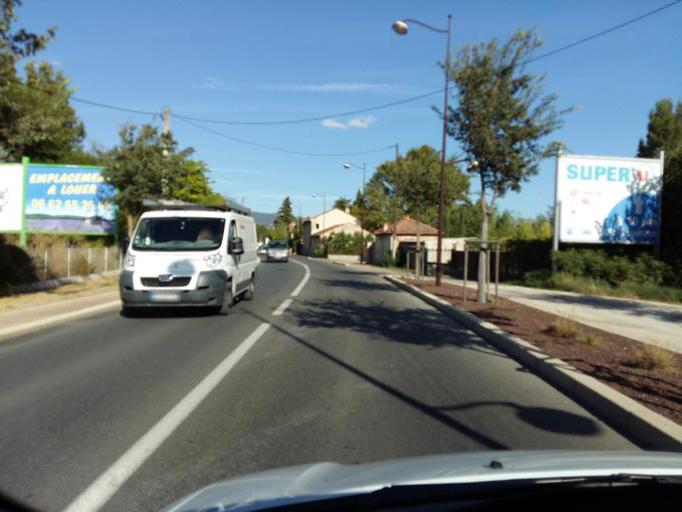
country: FR
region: Provence-Alpes-Cote d'Azur
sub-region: Departement du Vaucluse
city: L'Isle-sur-la-Sorgue
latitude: 43.9189
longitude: 5.0327
